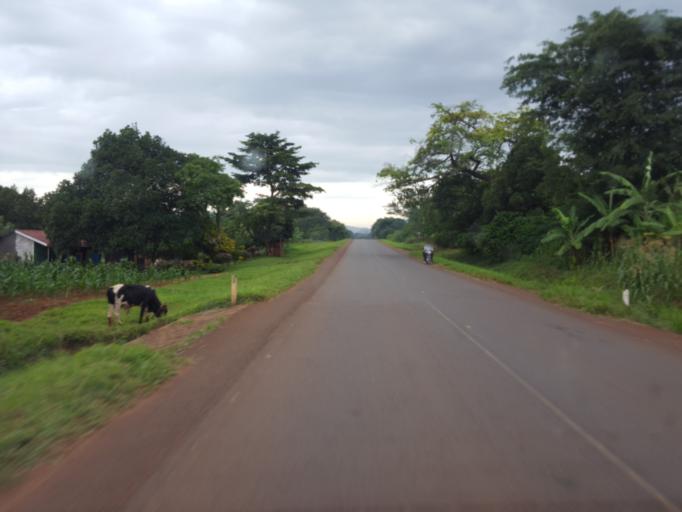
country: UG
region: Central Region
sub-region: Kiboga District
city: Kiboga
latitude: 0.8438
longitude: 31.8792
